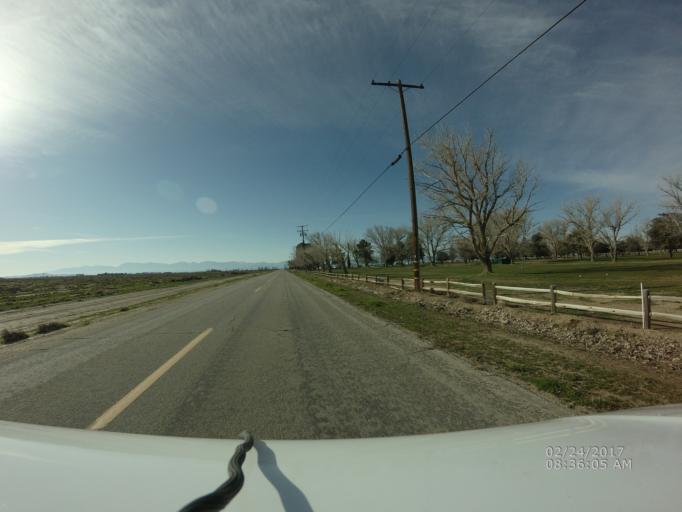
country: US
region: California
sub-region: Los Angeles County
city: Lancaster
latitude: 34.7437
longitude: -118.0233
